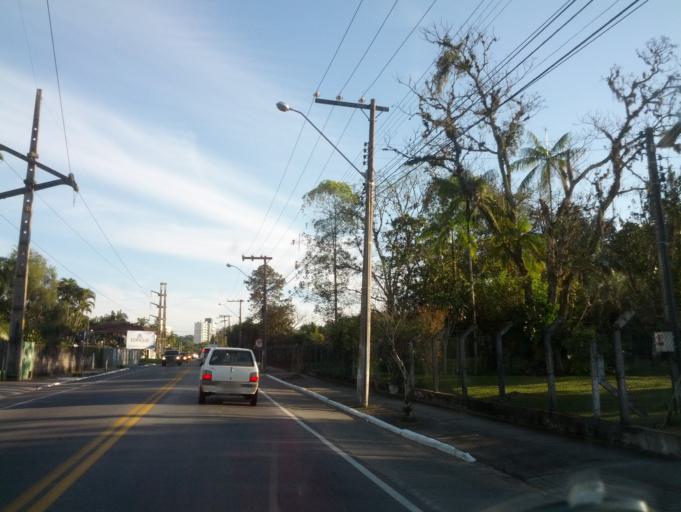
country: BR
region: Santa Catarina
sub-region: Indaial
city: Indaial
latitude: -26.8895
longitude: -49.2247
